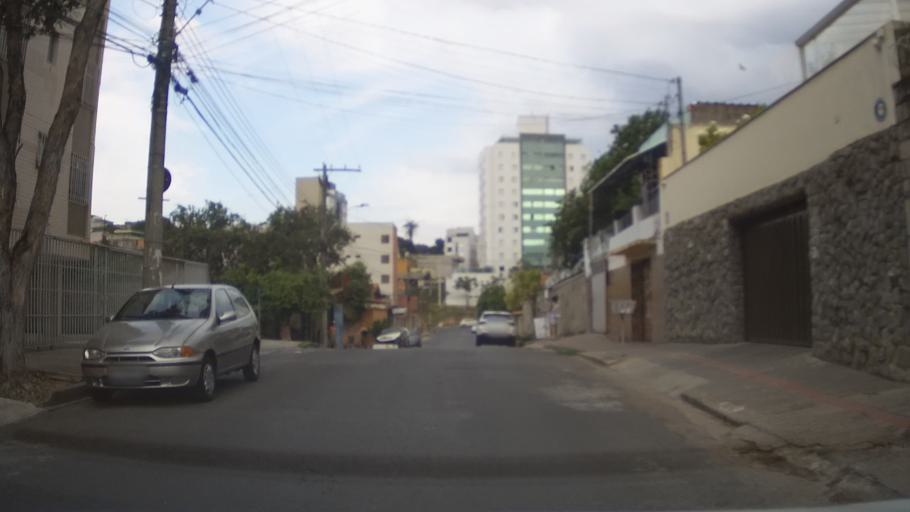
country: BR
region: Minas Gerais
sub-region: Belo Horizonte
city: Belo Horizonte
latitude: -19.8785
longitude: -43.9278
